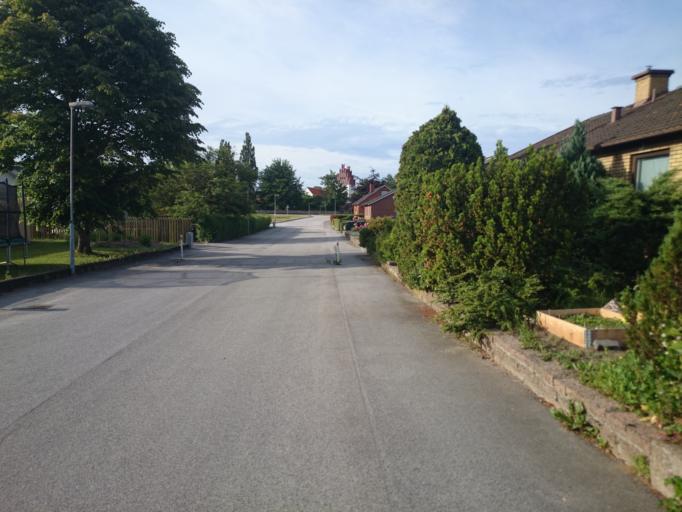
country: SE
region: Skane
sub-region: Eslovs Kommun
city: Eslov
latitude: 55.7240
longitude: 13.3403
